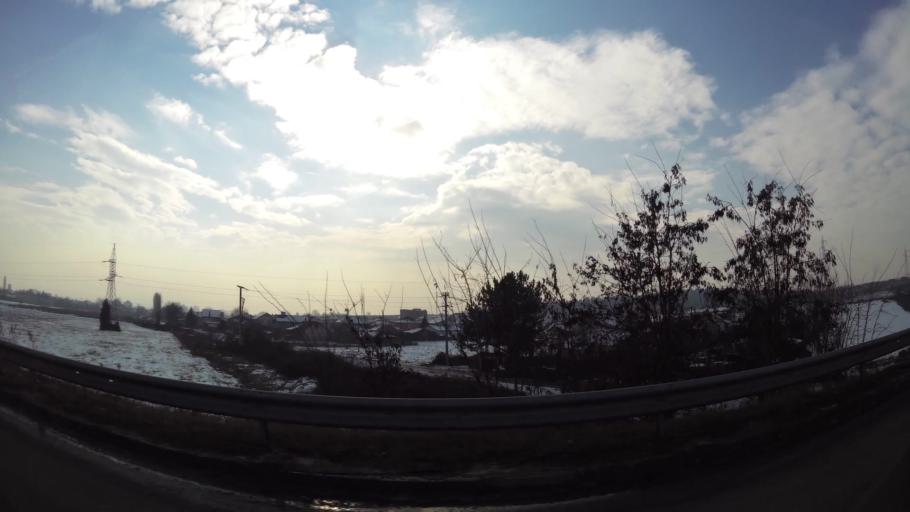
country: MK
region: Butel
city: Butel
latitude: 42.0448
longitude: 21.4429
